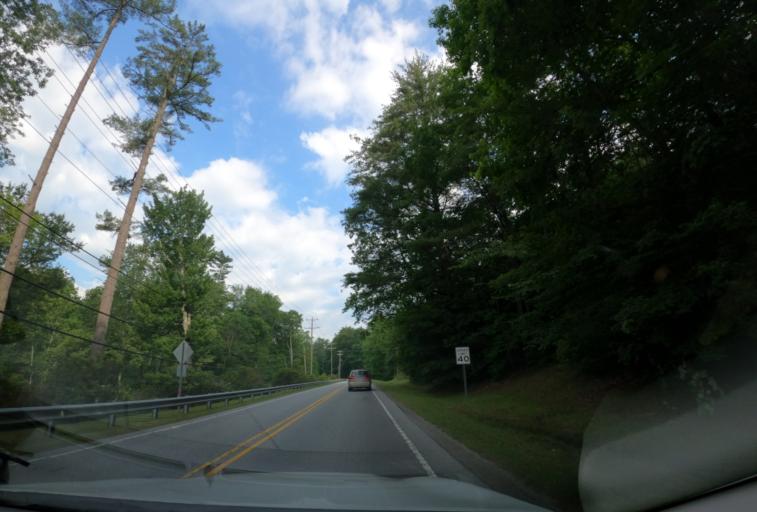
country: US
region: North Carolina
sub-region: Jackson County
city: Cullowhee
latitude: 35.1160
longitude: -83.0313
